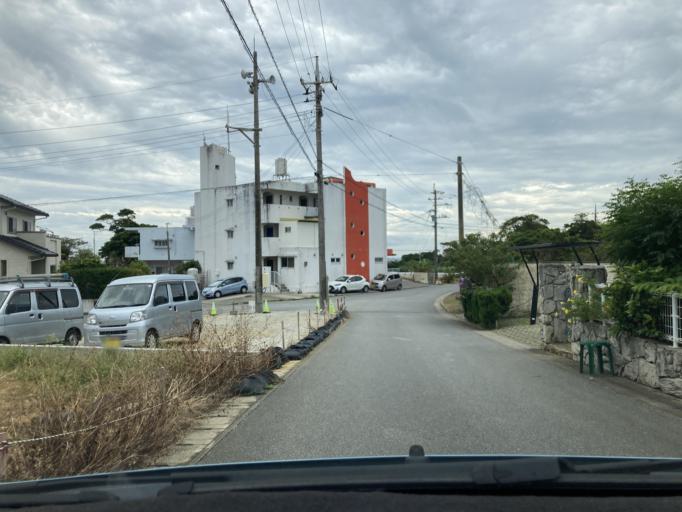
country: JP
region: Okinawa
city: Ishikawa
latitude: 26.4050
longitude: 127.7394
